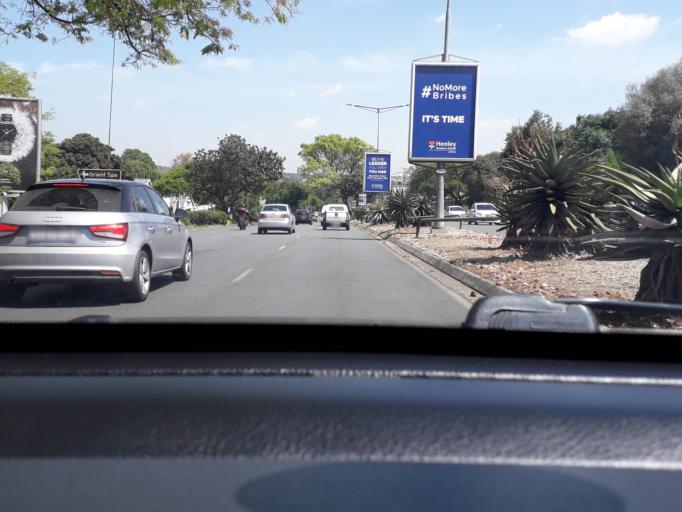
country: ZA
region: Gauteng
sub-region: City of Johannesburg Metropolitan Municipality
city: Johannesburg
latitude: -26.1022
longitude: 28.0404
